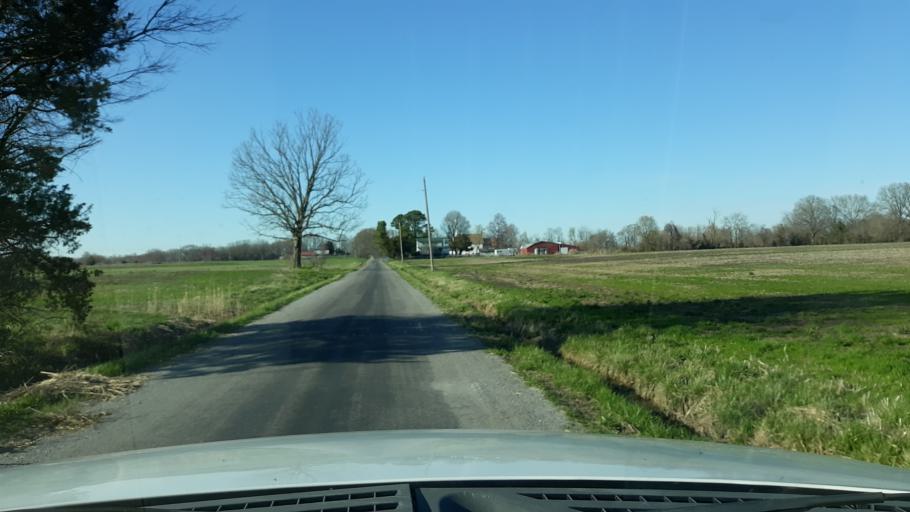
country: US
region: Illinois
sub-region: Saline County
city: Harrisburg
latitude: 37.8015
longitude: -88.6055
